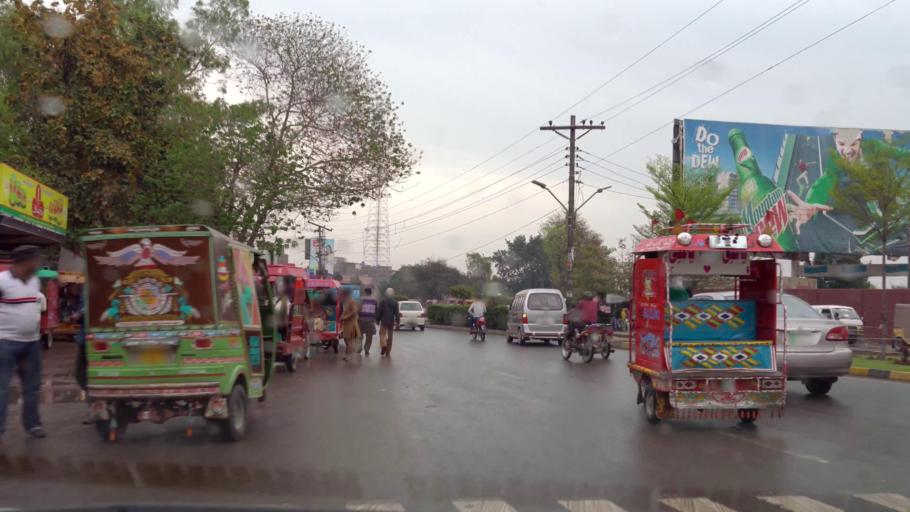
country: PK
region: Punjab
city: Faisalabad
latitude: 31.4172
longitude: 73.0914
